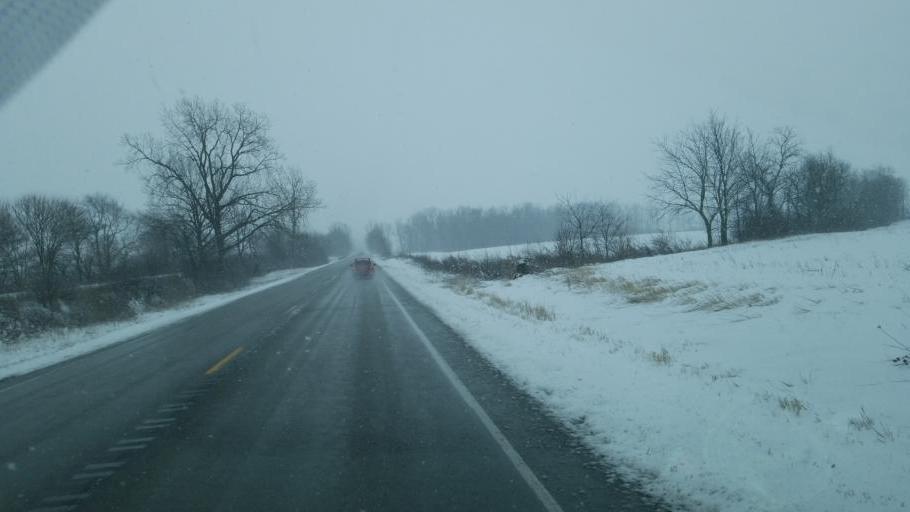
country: US
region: Indiana
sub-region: Wayne County
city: Hagerstown
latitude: 40.0434
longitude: -85.2139
